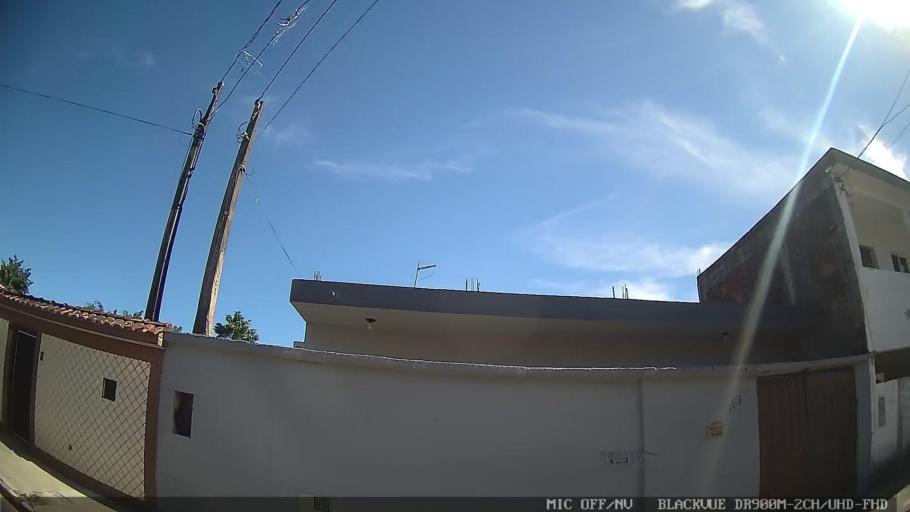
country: BR
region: Sao Paulo
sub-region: Santos
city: Santos
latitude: -23.9422
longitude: -46.2856
